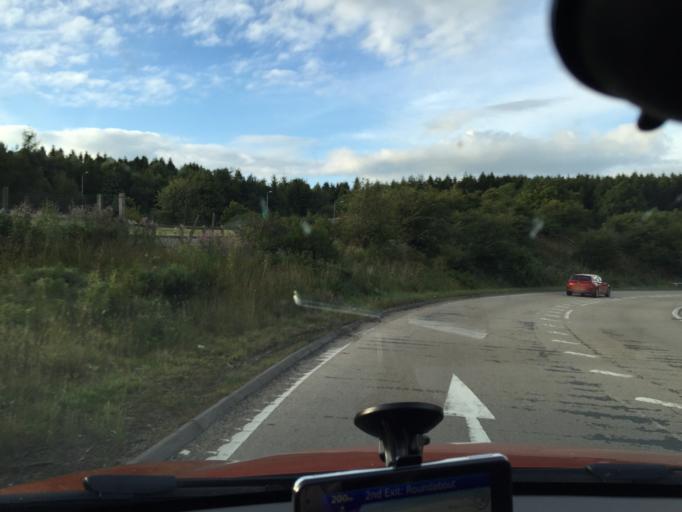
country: GB
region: Scotland
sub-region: North Lanarkshire
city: Cumbernauld
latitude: 55.9665
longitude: -3.9753
